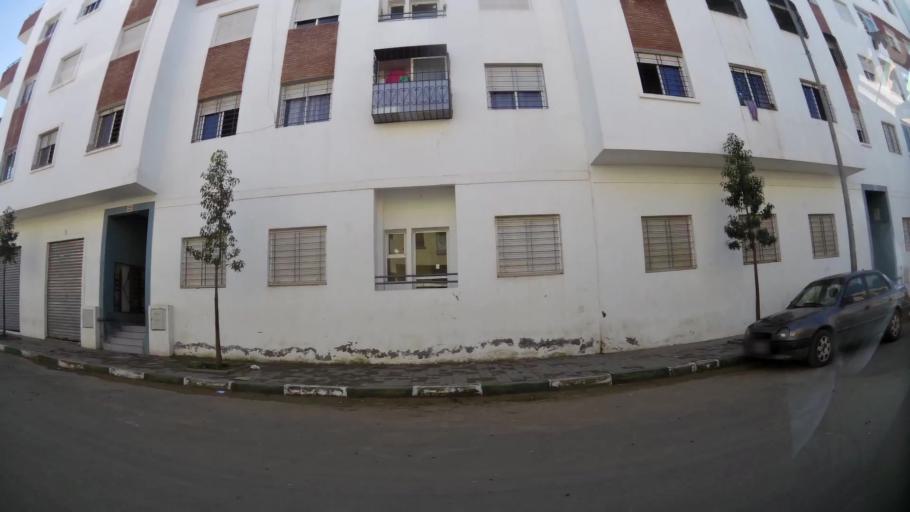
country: MA
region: Grand Casablanca
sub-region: Mediouna
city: Mediouna
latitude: 33.4551
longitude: -7.5081
